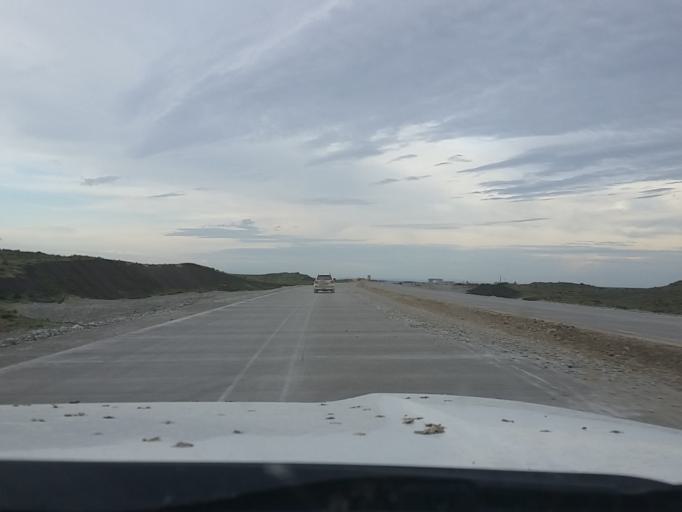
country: KZ
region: Almaty Oblysy
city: Zharkent
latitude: 44.1741
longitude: 80.3349
